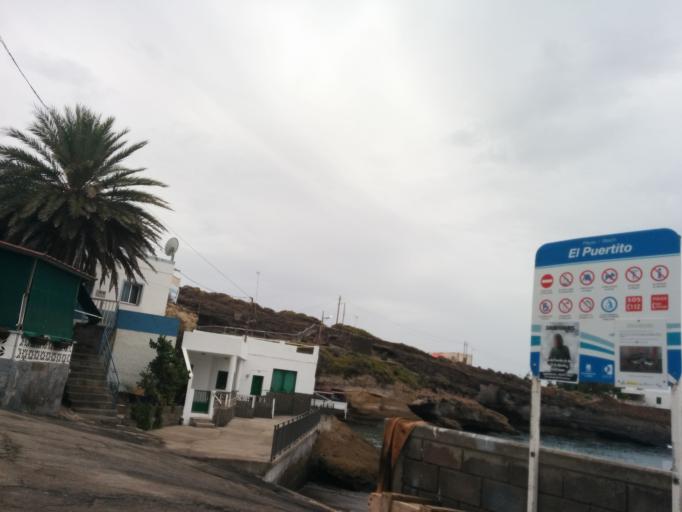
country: ES
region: Canary Islands
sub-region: Provincia de Santa Cruz de Tenerife
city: Adeje
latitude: 28.1135
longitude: -16.7679
